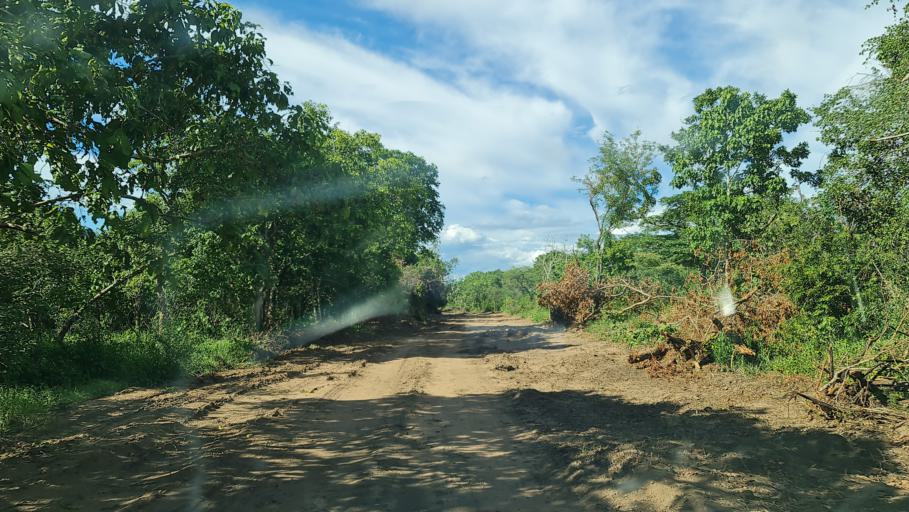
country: MZ
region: Nampula
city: Antonio Enes
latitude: -15.5172
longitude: 40.1298
